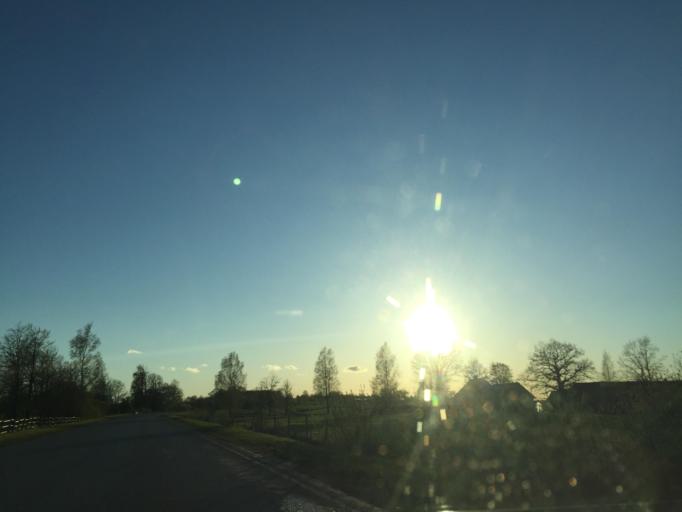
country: LV
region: Skriveri
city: Skriveri
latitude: 56.8845
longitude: 25.2216
